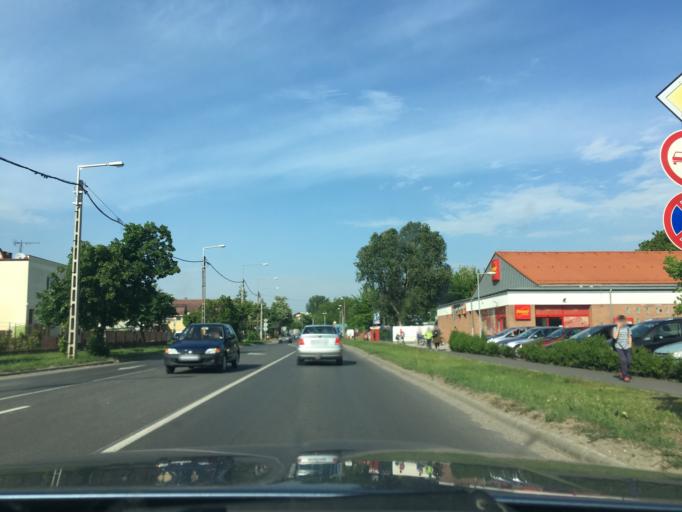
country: HU
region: Hajdu-Bihar
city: Debrecen
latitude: 47.5488
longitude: 21.6589
